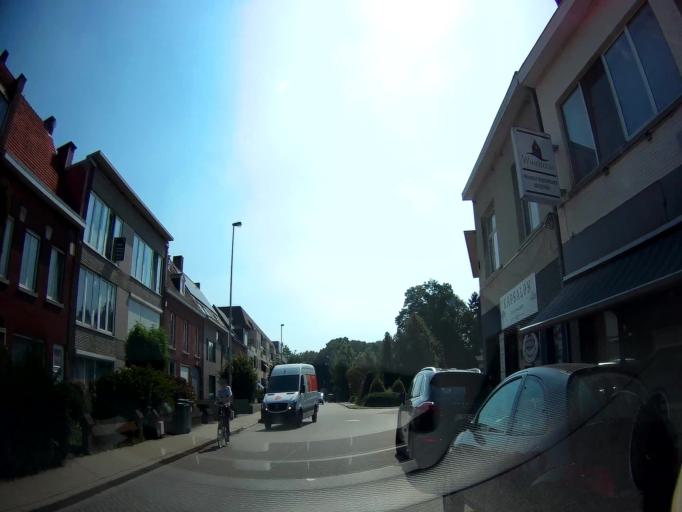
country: BE
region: Flanders
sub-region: Provincie Antwerpen
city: Turnhout
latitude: 51.3145
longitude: 4.9441
